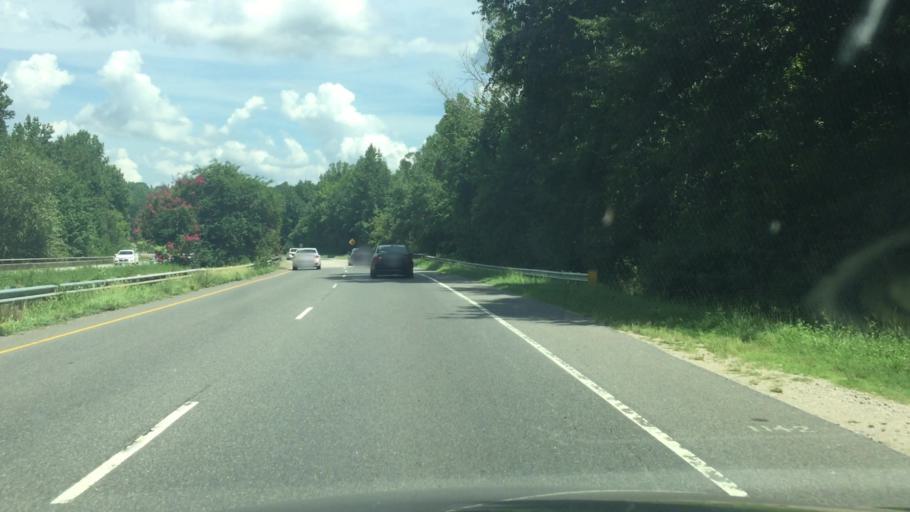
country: US
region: North Carolina
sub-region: Richmond County
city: Rockingham
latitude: 34.9450
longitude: -79.7753
